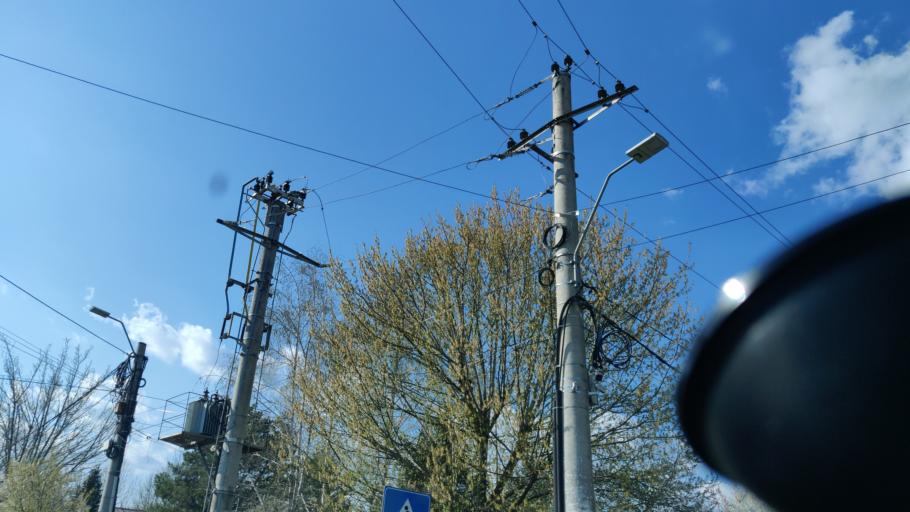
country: RO
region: Ilfov
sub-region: Comuna Magurele
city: Magurele
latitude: 44.3528
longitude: 26.0394
